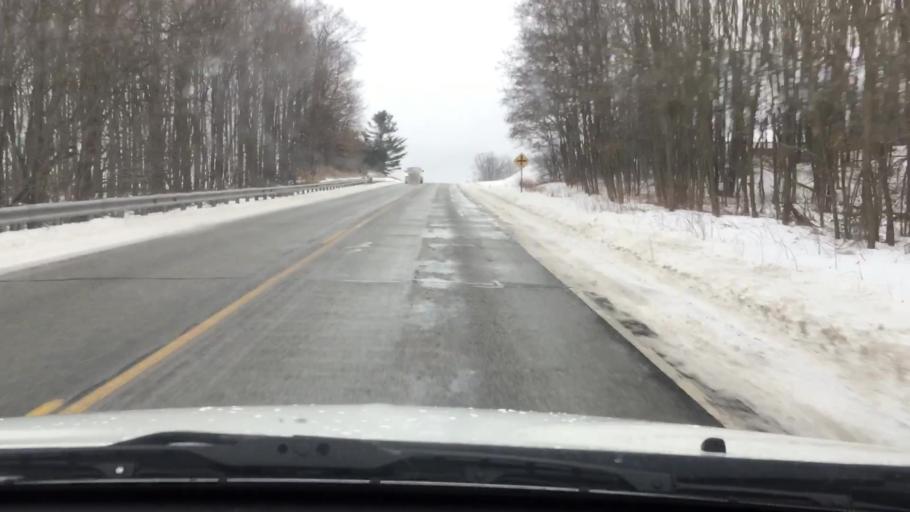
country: US
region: Michigan
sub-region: Wexford County
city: Cadillac
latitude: 44.1681
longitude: -85.4054
